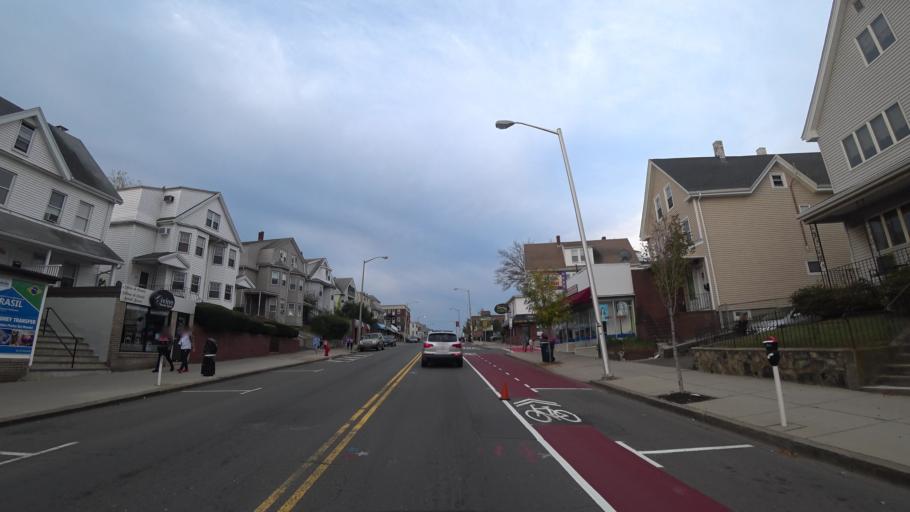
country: US
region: Massachusetts
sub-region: Middlesex County
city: Everett
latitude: 42.4143
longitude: -71.0490
